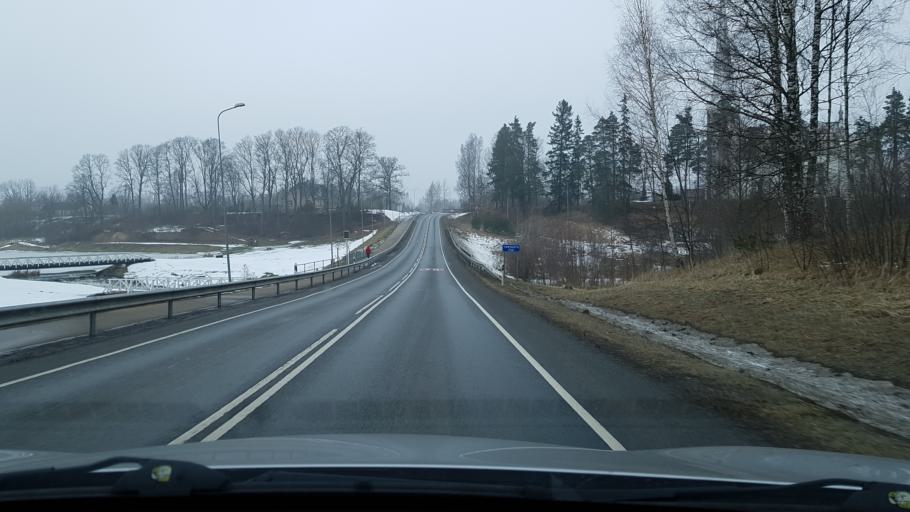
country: EE
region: Valgamaa
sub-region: Torva linn
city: Torva
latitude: 58.2281
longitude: 25.8854
